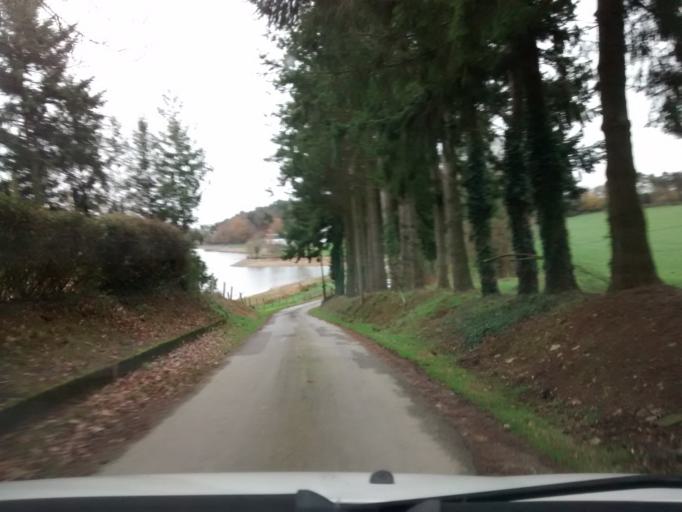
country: FR
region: Brittany
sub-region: Departement d'Ille-et-Vilaine
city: Erbree
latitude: 48.0977
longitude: -1.1569
